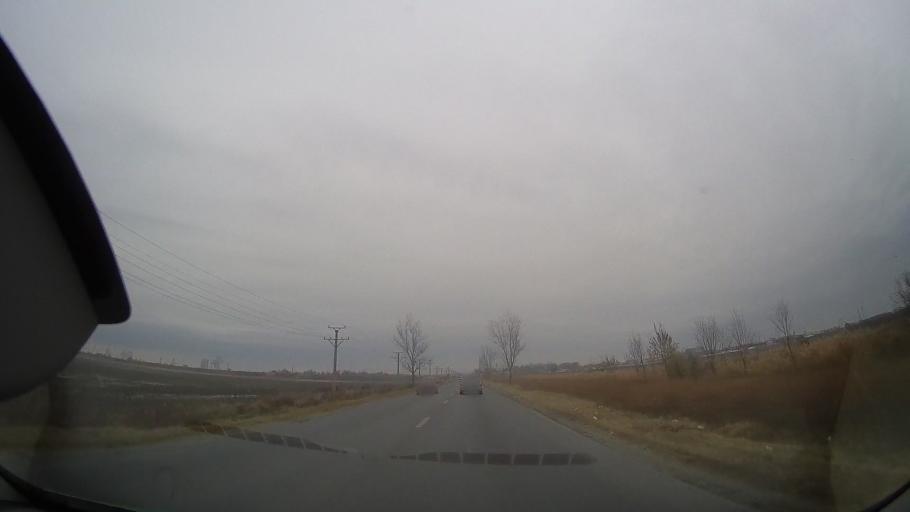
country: RO
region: Ialomita
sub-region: Comuna Slobozia
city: Slobozia
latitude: 44.5823
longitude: 27.3359
